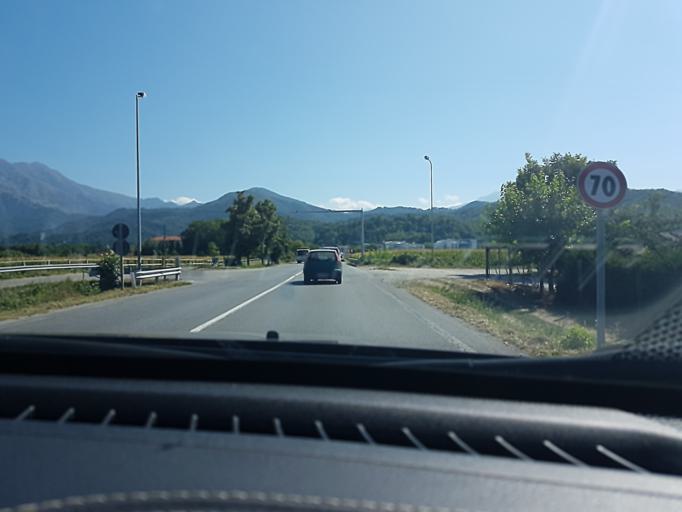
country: IT
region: Piedmont
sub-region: Provincia di Cuneo
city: Boves
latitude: 44.3422
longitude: 7.5453
